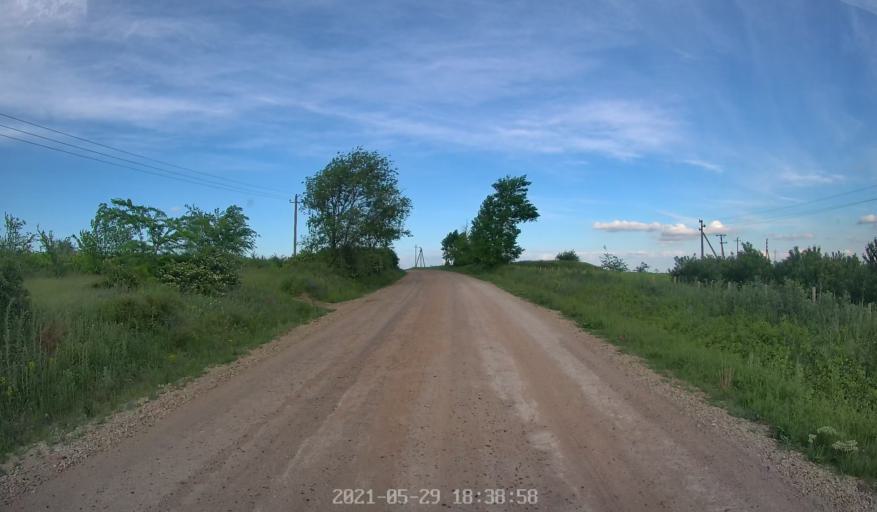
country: MD
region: Chisinau
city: Singera
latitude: 46.8011
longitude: 28.9412
